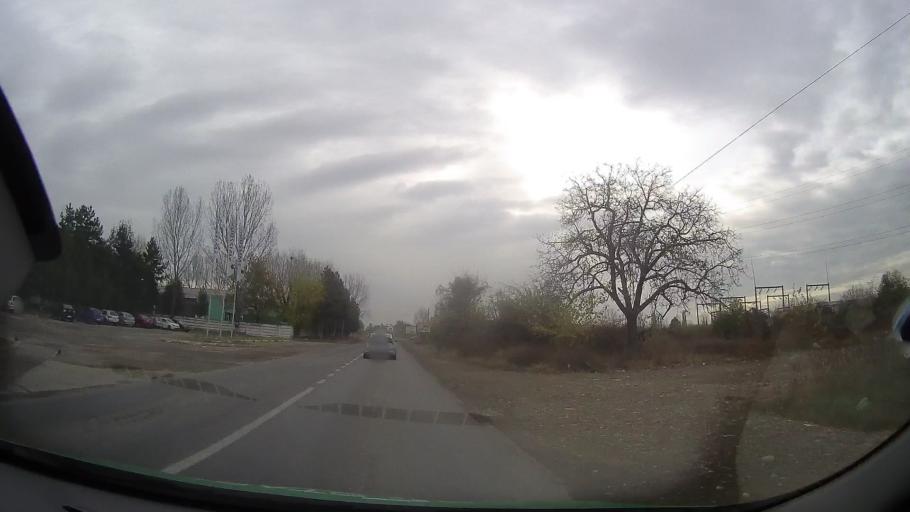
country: RO
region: Prahova
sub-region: Comuna Berceni
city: Berceni
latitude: 44.9442
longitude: 26.1006
